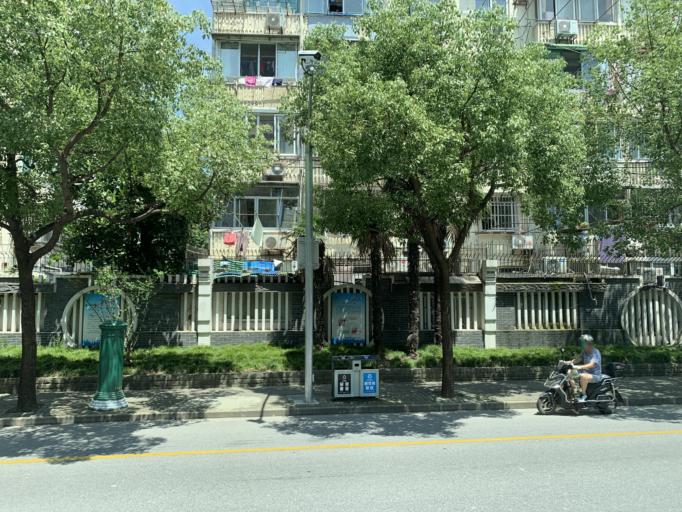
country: CN
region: Shanghai Shi
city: Pudong
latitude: 31.2355
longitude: 121.5205
